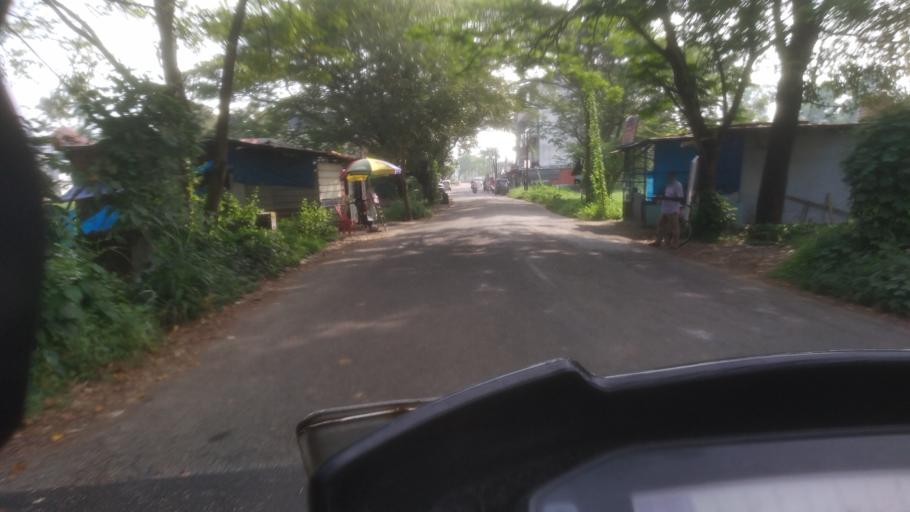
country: IN
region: Kerala
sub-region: Ernakulam
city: Angamali
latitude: 10.1616
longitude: 76.3805
